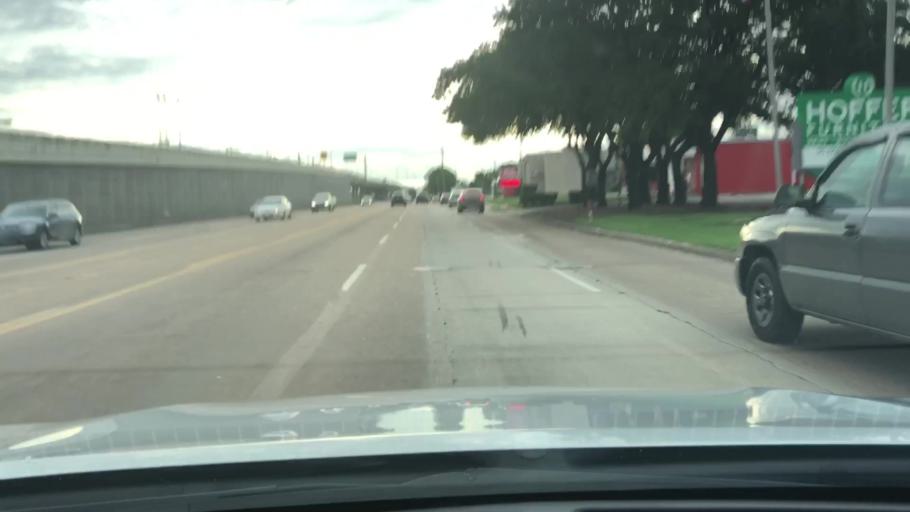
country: US
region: Texas
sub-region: Harris County
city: Piney Point Village
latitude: 29.7225
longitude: -95.5082
